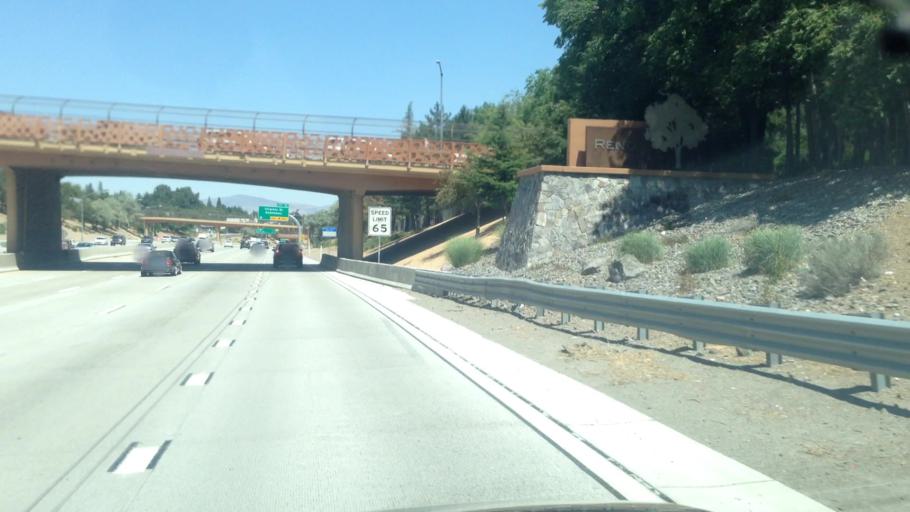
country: US
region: Nevada
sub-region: Washoe County
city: Reno
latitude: 39.5322
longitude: -119.8227
